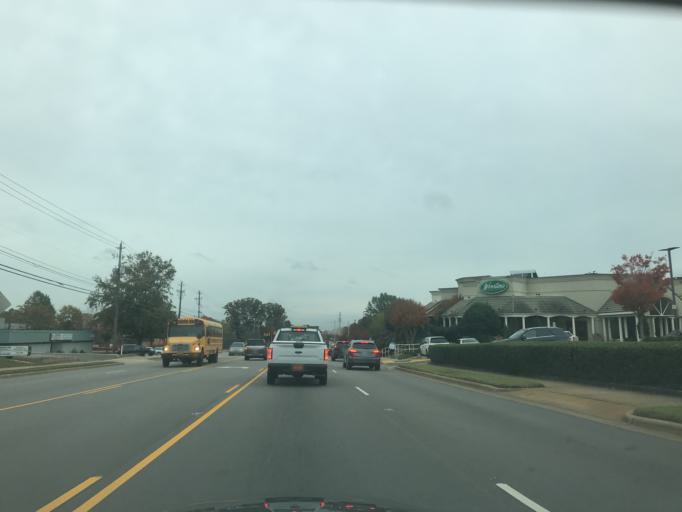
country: US
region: North Carolina
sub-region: Wake County
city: West Raleigh
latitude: 35.8703
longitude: -78.6215
